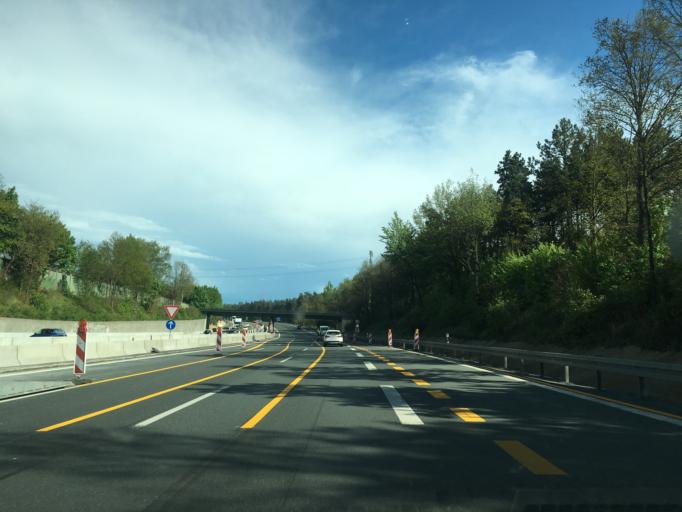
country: DE
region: Bavaria
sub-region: Regierungsbezirk Mittelfranken
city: Schwaig
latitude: 49.4694
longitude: 11.1860
